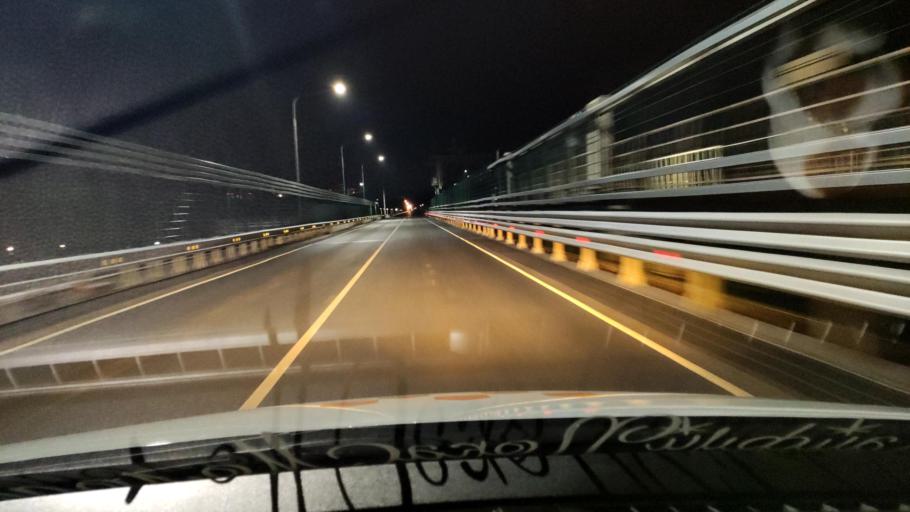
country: RU
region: Voronezj
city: Shilovo
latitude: 51.5384
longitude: 39.1387
